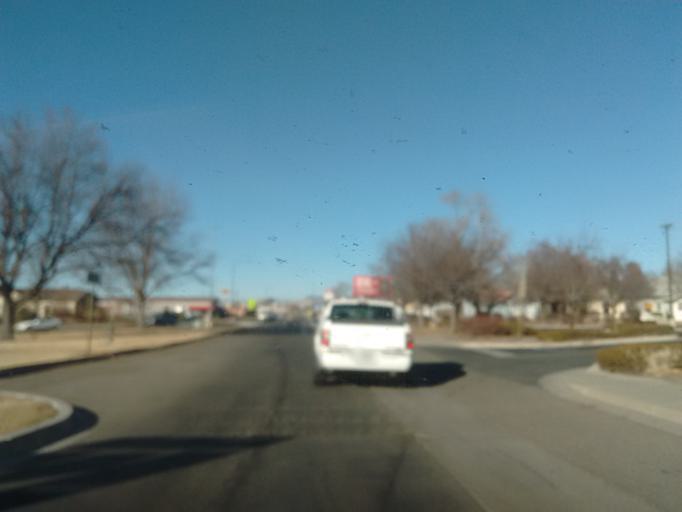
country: US
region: Colorado
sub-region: Mesa County
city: Grand Junction
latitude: 39.0708
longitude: -108.5708
